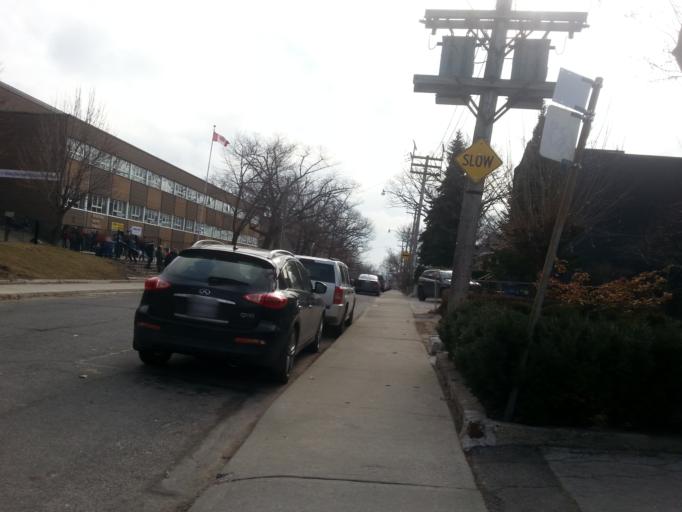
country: CA
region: Ontario
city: Toronto
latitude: 43.6778
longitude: -79.4315
